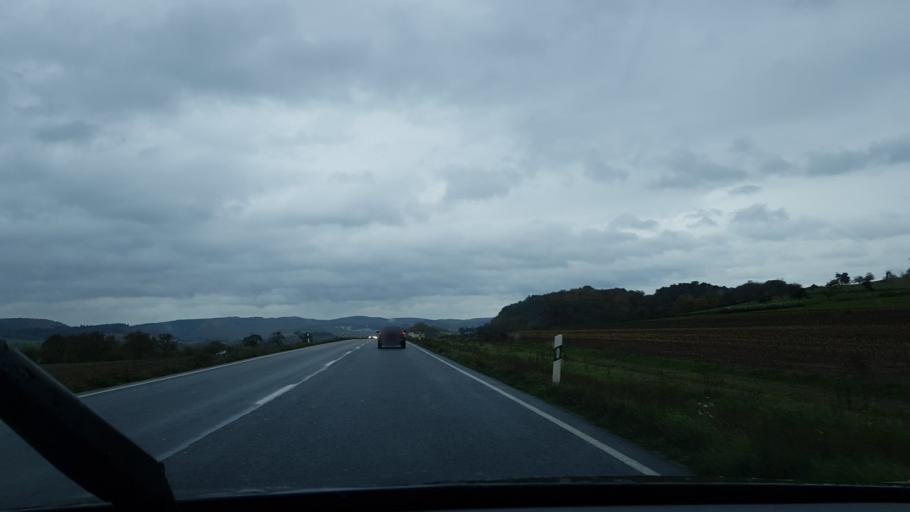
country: DE
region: Rheinland-Pfalz
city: Salmtal
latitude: 49.9626
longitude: 6.8541
